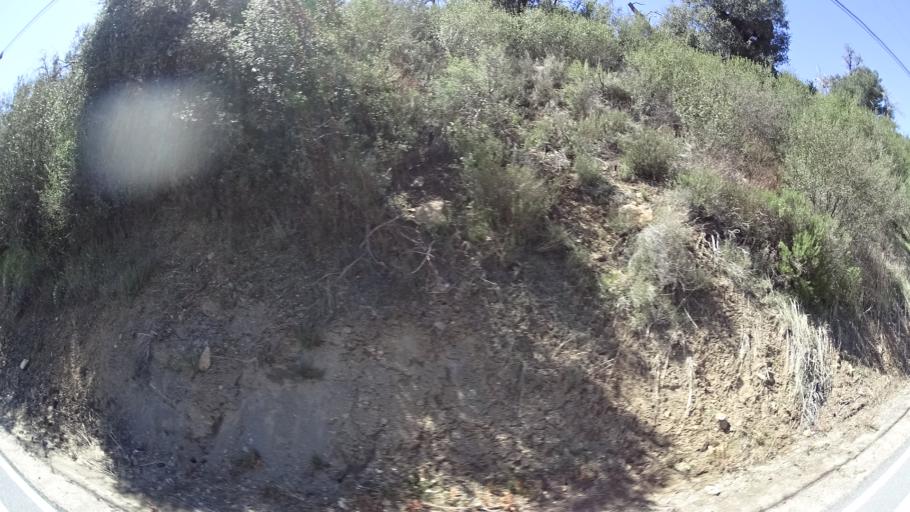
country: US
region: California
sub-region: San Diego County
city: Descanso
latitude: 32.9421
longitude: -116.5671
